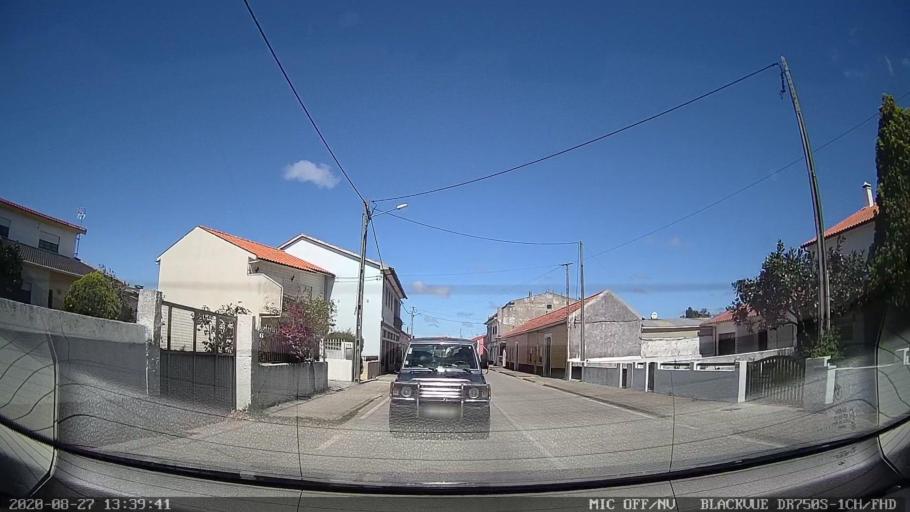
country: PT
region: Coimbra
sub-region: Mira
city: Mira
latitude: 40.4394
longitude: -8.7282
